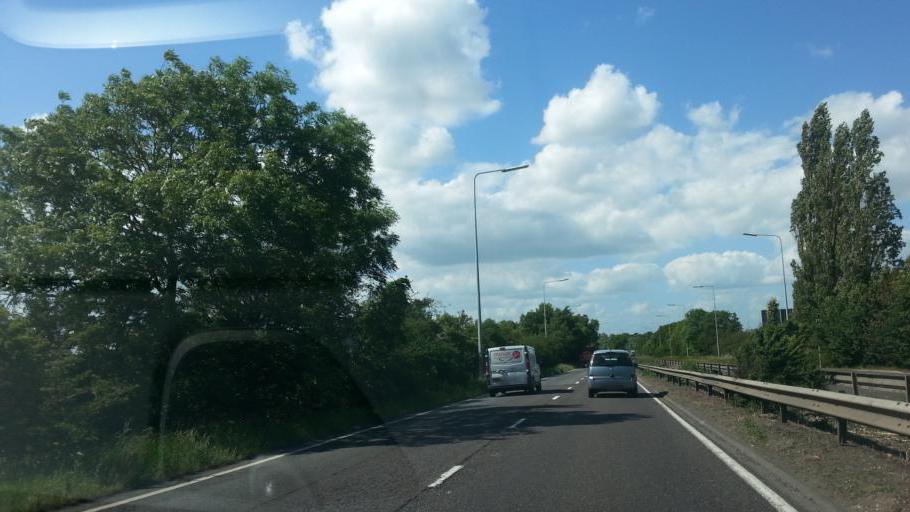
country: GB
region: England
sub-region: Central Bedfordshire
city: Astwick
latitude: 52.0343
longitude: -0.2178
